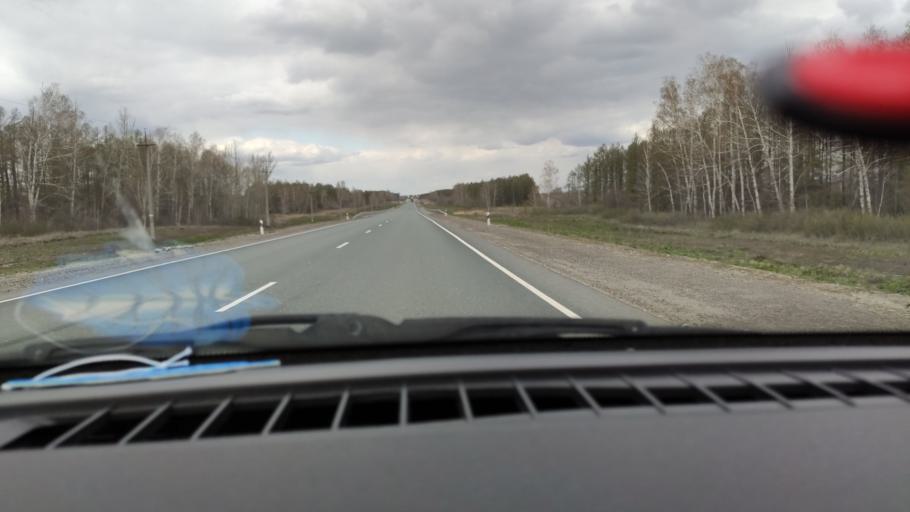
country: RU
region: Saratov
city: Shikhany
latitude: 52.1545
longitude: 47.1805
